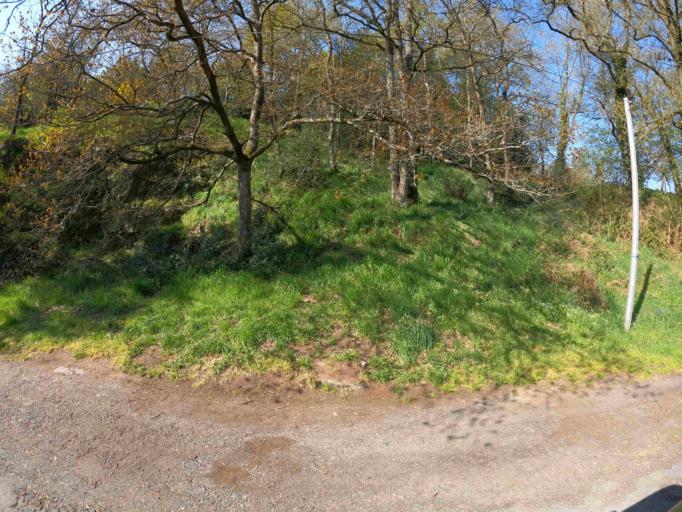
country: FR
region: Pays de la Loire
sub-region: Departement de la Loire-Atlantique
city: Remouille
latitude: 47.0695
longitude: -1.3871
